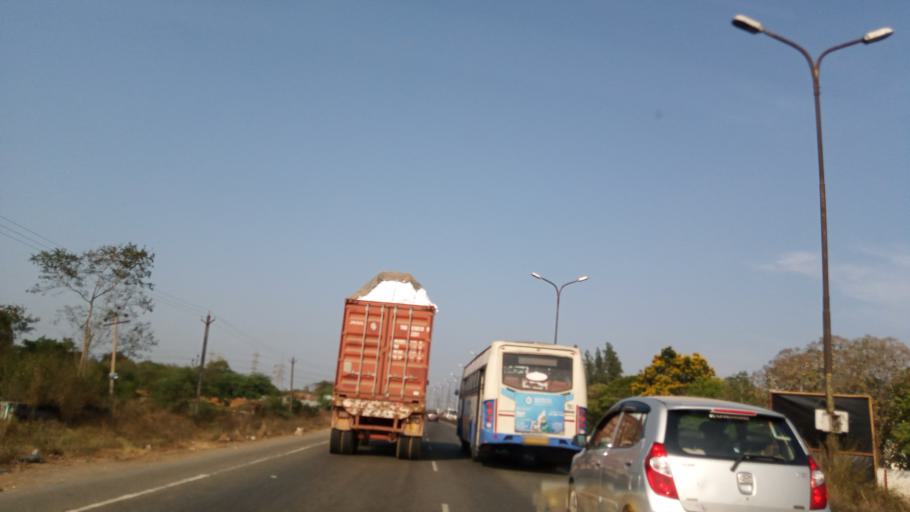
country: IN
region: Tamil Nadu
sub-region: Kancheepuram
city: Sriperumbudur
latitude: 12.9836
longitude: 79.9725
